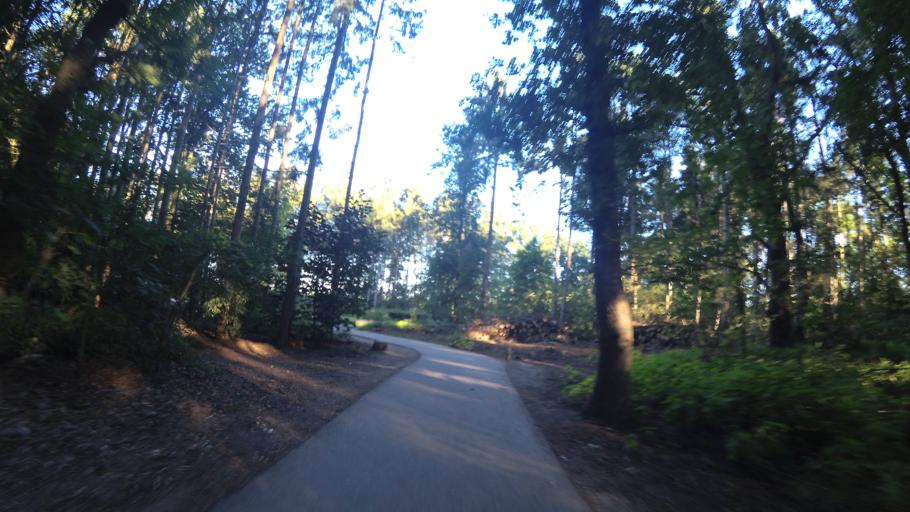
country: NL
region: North Brabant
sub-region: Gemeente Loon op Zand
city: Loon op Zand
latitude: 51.6483
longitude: 5.0409
